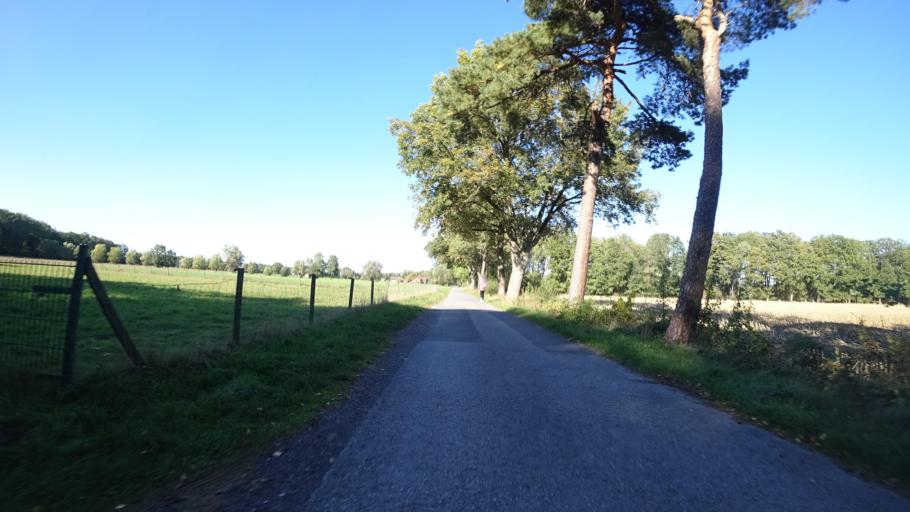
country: DE
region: North Rhine-Westphalia
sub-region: Regierungsbezirk Detmold
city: Guetersloh
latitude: 51.8670
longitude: 8.3670
